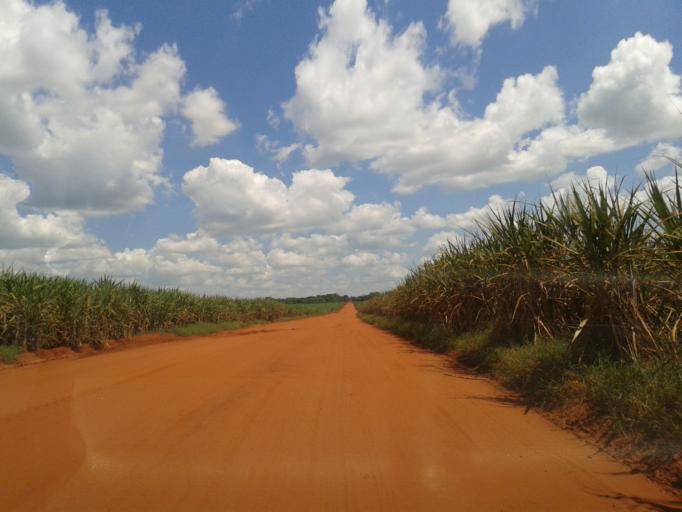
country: BR
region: Minas Gerais
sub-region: Ituiutaba
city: Ituiutaba
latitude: -19.0525
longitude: -49.7156
